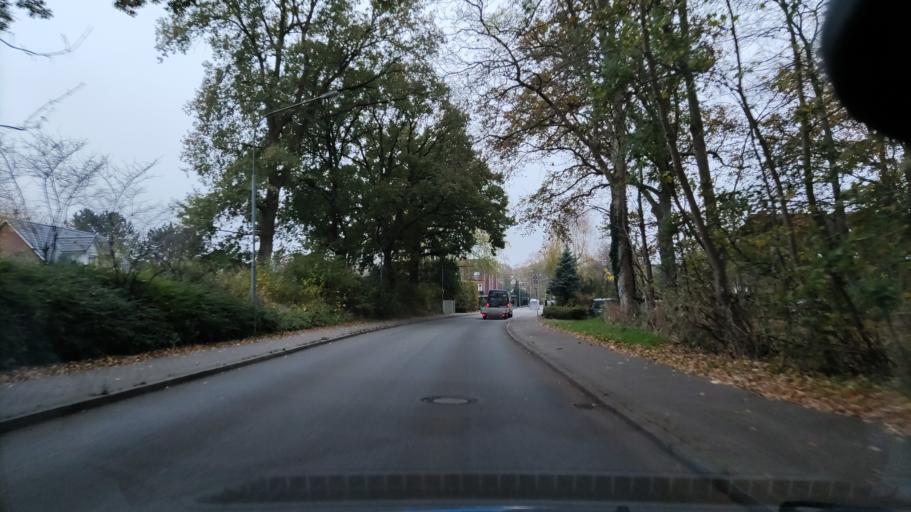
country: DE
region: Schleswig-Holstein
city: Gross Gronau
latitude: 53.8209
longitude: 10.7192
